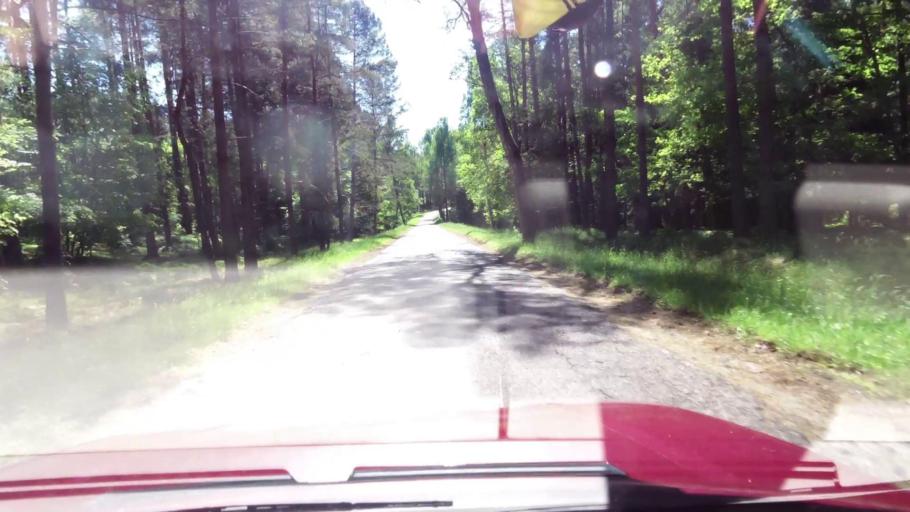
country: PL
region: West Pomeranian Voivodeship
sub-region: Powiat koszalinski
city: Bobolice
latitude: 54.0626
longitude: 16.5684
